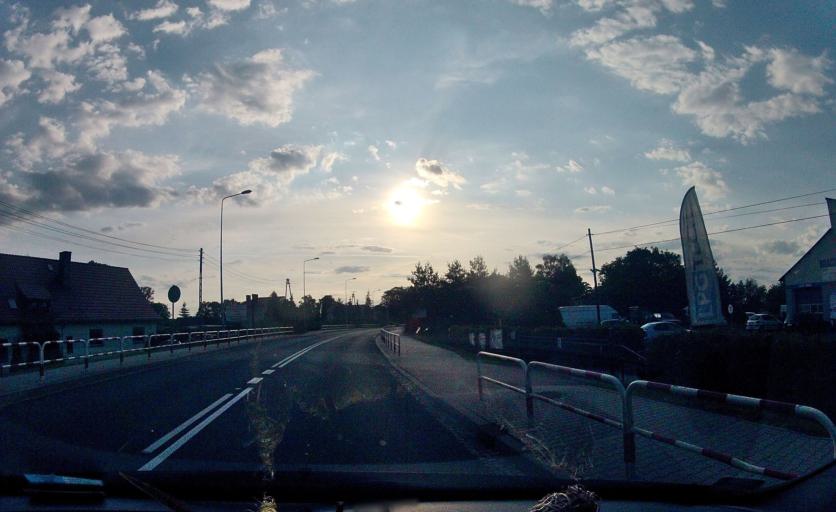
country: PL
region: Opole Voivodeship
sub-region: Powiat kluczborski
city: Kluczbork
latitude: 50.9736
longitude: 18.2492
